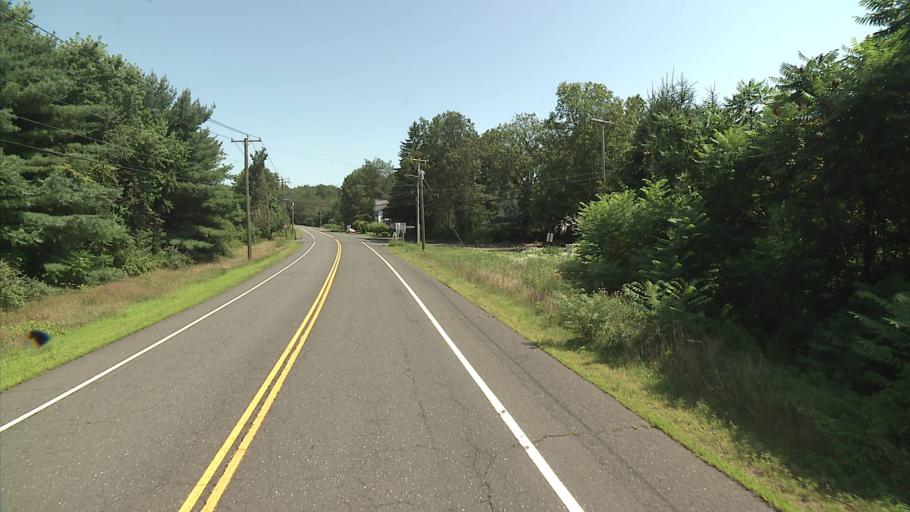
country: US
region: Connecticut
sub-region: Hartford County
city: North Granby
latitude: 41.9566
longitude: -72.8407
